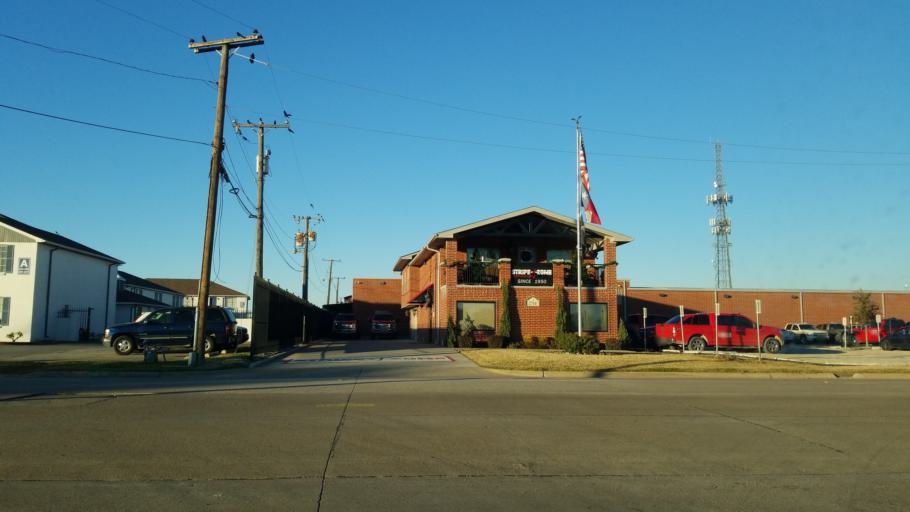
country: US
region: Texas
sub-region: Dallas County
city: Grand Prairie
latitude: 32.7350
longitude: -97.0484
